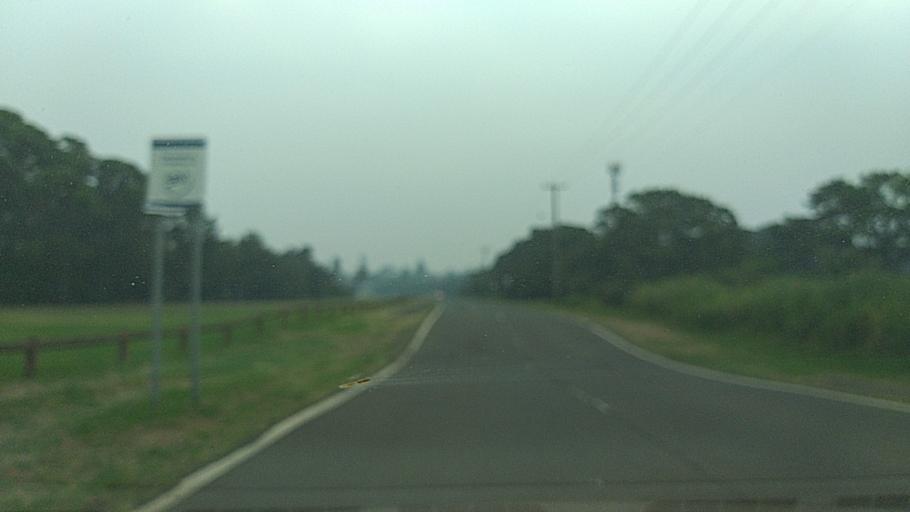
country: AU
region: New South Wales
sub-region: Shellharbour
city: Barrack Heights
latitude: -34.5669
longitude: 150.8666
